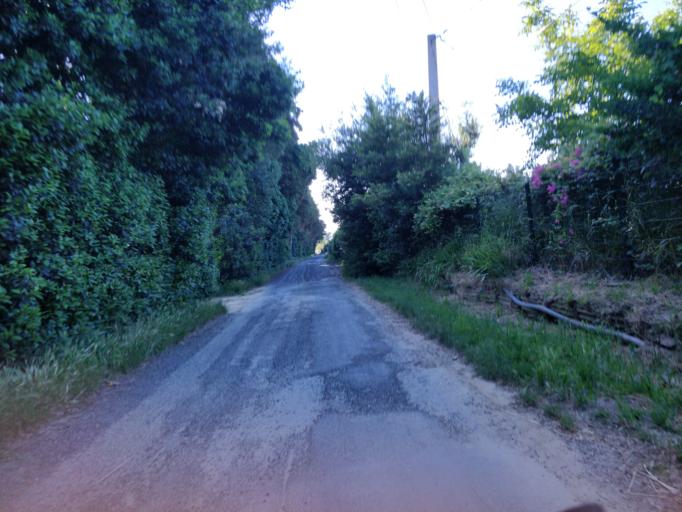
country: FR
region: Languedoc-Roussillon
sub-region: Departement des Pyrenees-Orientales
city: Elne
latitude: 42.6056
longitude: 2.9610
